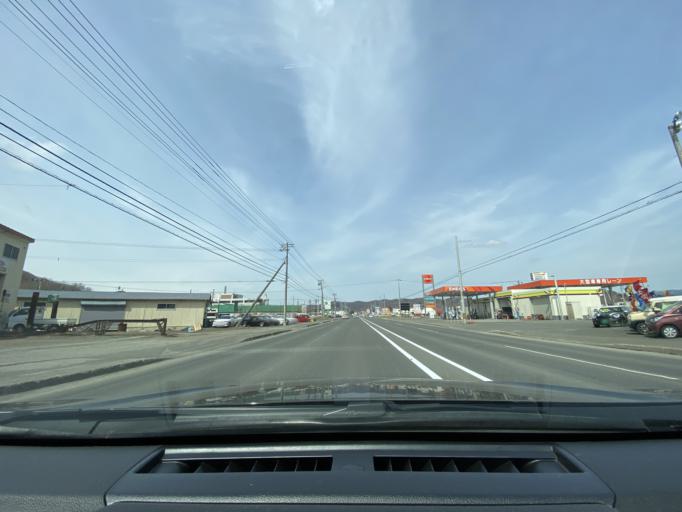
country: JP
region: Hokkaido
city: Kitami
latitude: 43.8019
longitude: 143.8193
